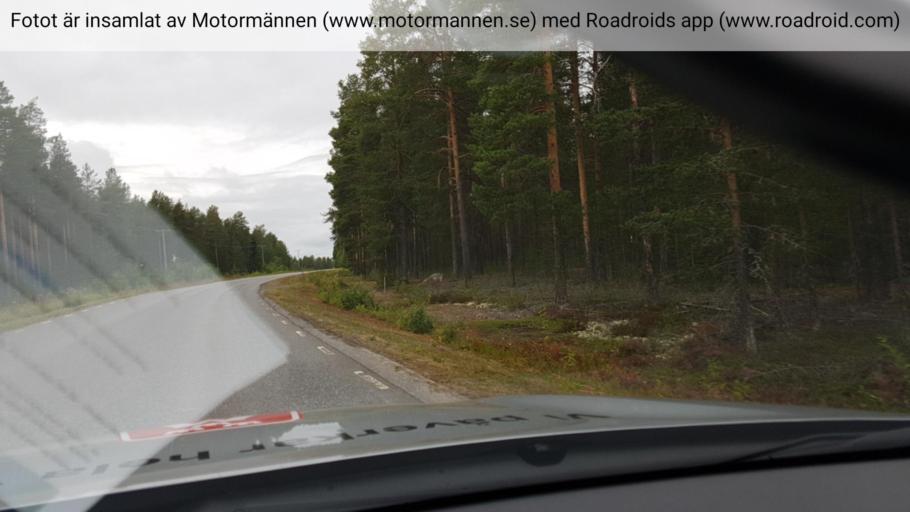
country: SE
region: Norrbotten
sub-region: Bodens Kommun
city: Boden
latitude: 65.8150
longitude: 21.5993
